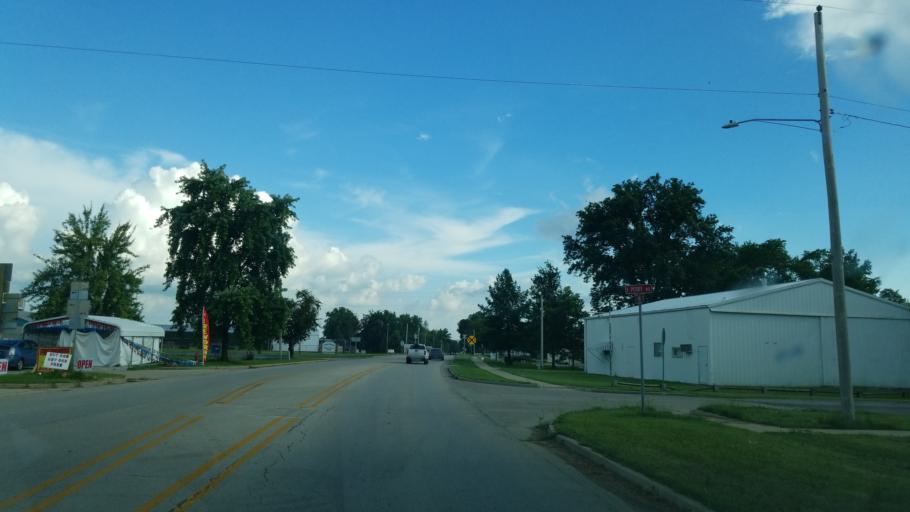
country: US
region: Illinois
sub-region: Marion County
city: Sandoval
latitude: 38.6151
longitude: -89.1143
